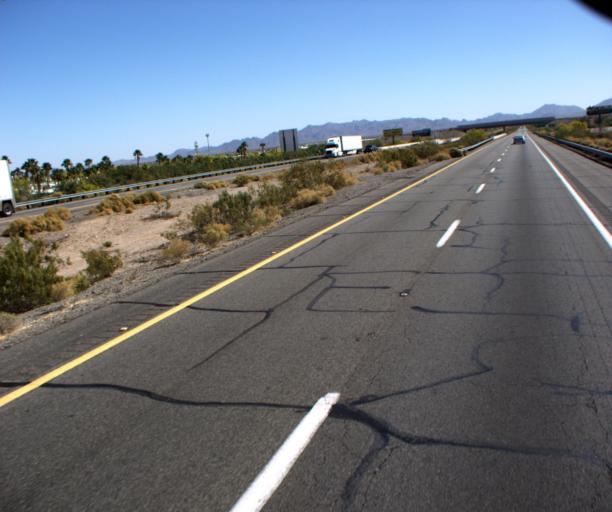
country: US
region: Arizona
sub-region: La Paz County
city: Quartzsite
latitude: 33.6620
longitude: -114.2239
